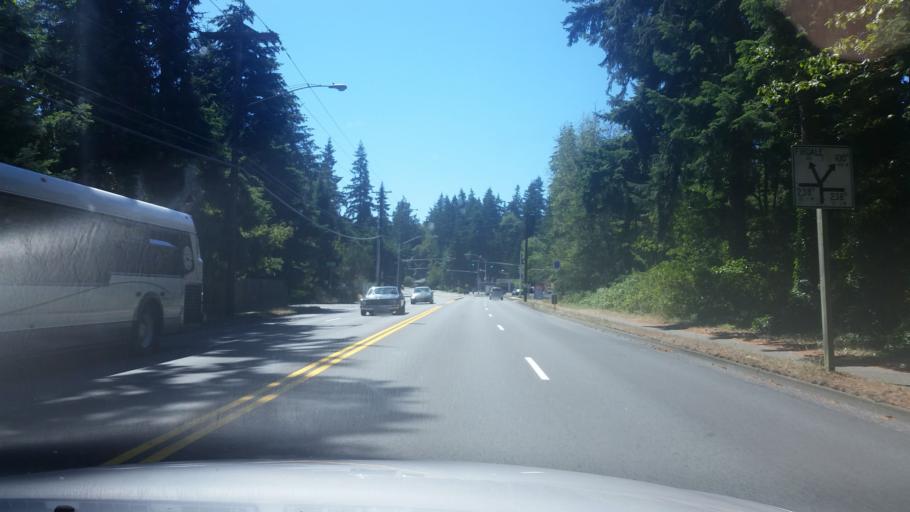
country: US
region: Washington
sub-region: Snohomish County
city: Esperance
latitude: 47.7845
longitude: -122.3665
